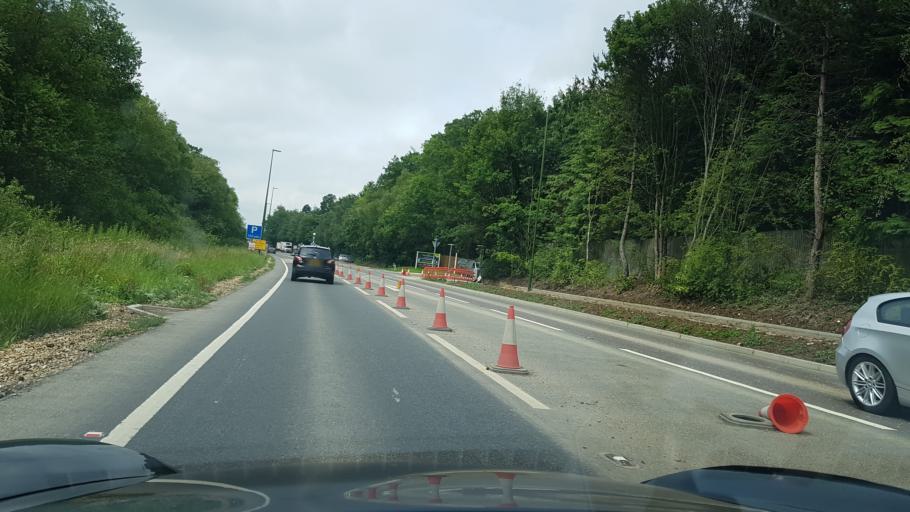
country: GB
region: England
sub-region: West Sussex
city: Copthorne
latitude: 51.1335
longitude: -0.1290
